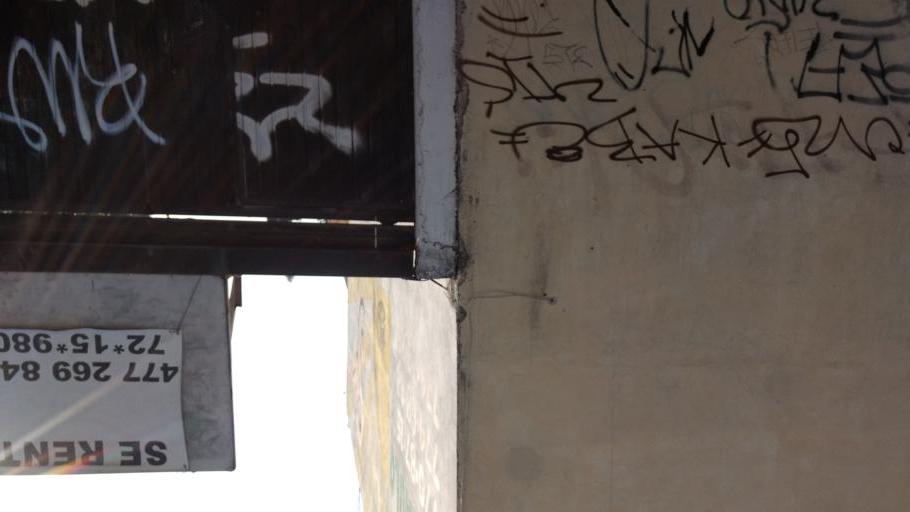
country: MX
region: Guanajuato
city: Leon
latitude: 21.1556
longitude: -101.6719
